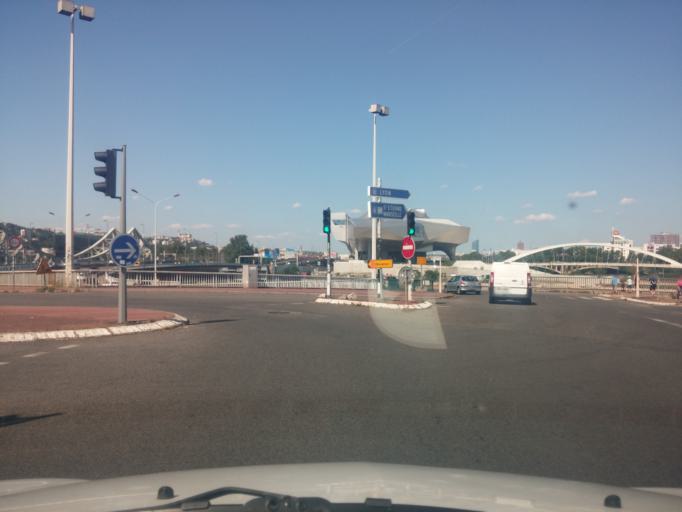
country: FR
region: Rhone-Alpes
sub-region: Departement du Rhone
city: La Mulatiere
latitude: 45.7293
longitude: 4.8157
